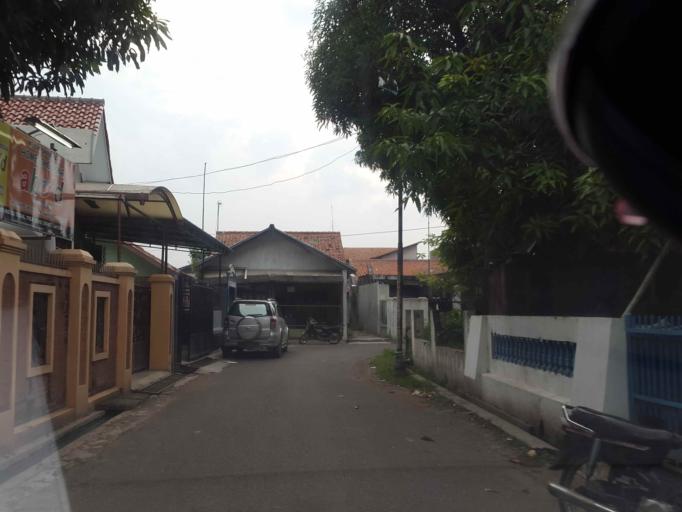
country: ID
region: Central Java
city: Tegal
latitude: -6.8732
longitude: 109.1303
